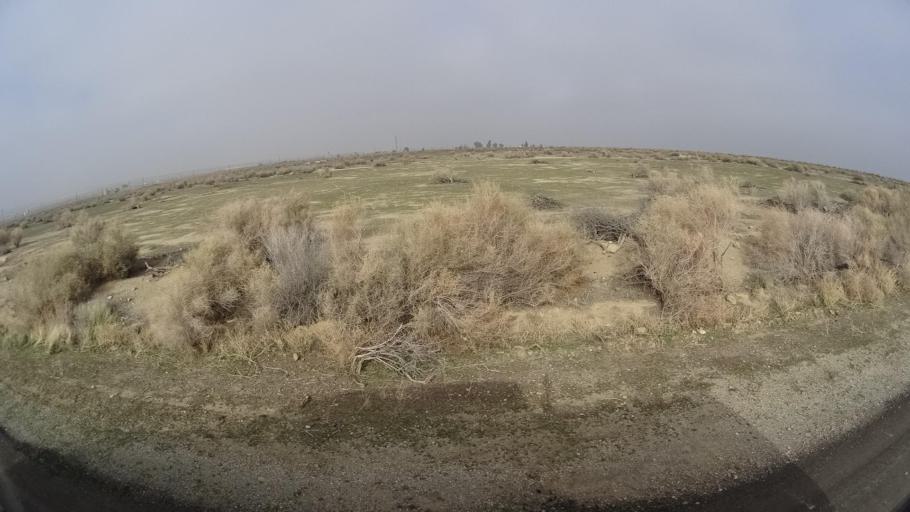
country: US
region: California
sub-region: Kern County
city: Maricopa
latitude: 35.0471
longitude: -119.3516
